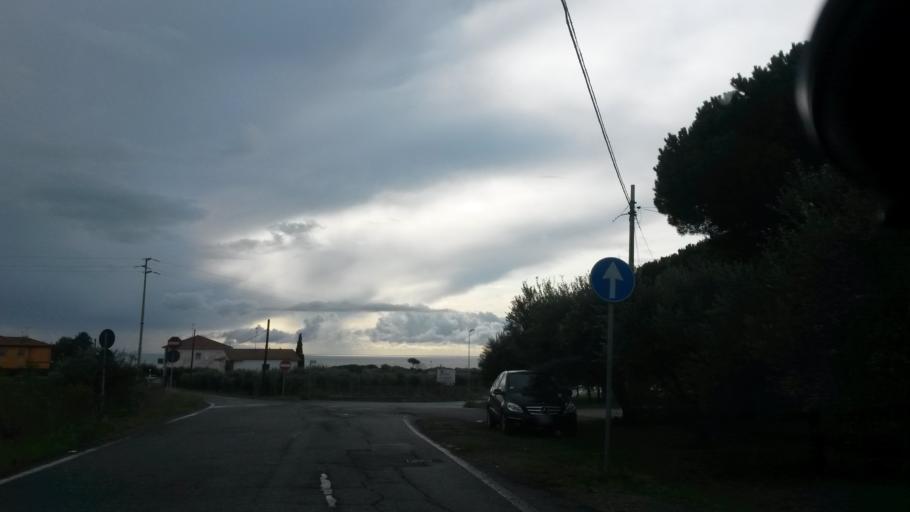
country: IT
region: Tuscany
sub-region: Provincia di Livorno
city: Rosignano Solvay-Castiglioncello
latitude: 43.4064
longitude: 10.4477
